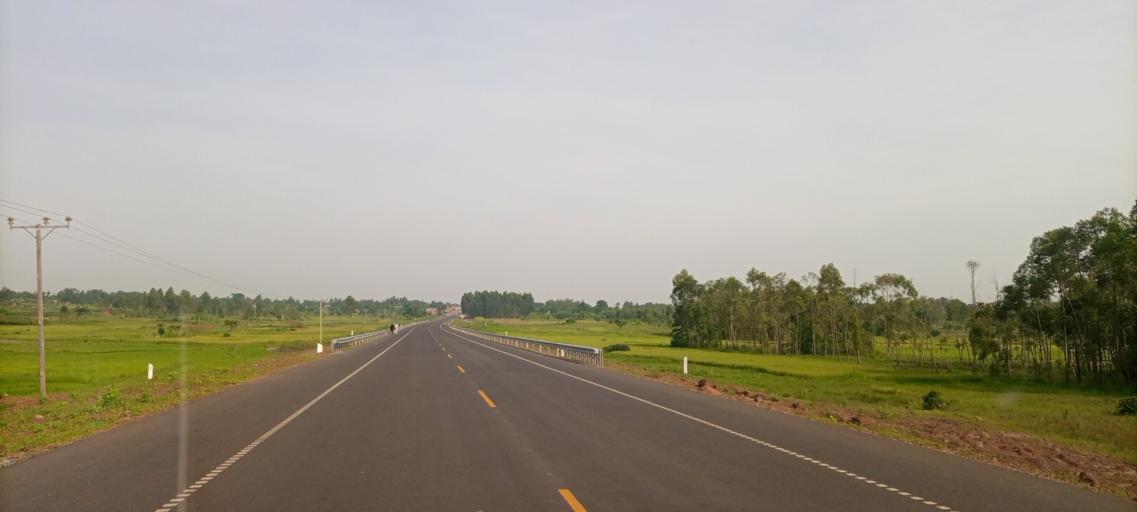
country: UG
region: Eastern Region
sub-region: Mbale District
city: Mbale
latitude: 1.0907
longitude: 34.0426
